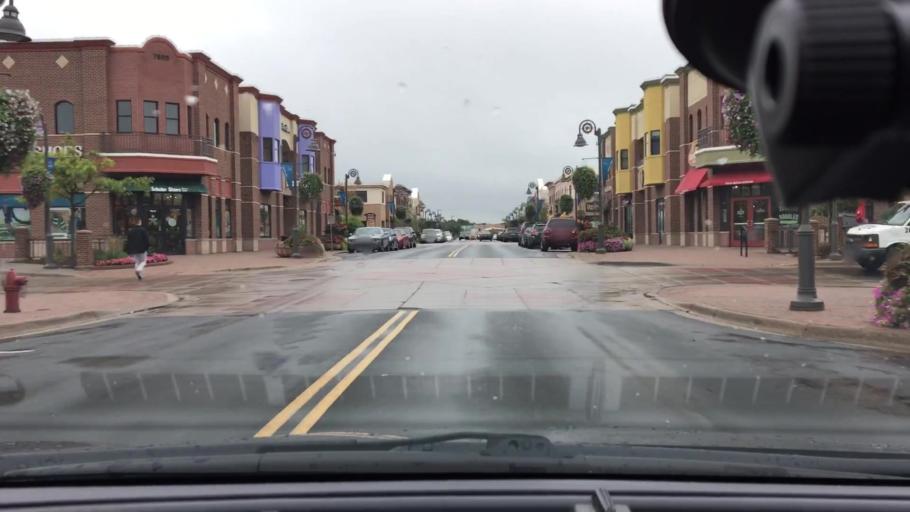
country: US
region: Minnesota
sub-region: Hennepin County
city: Maple Grove
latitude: 45.0964
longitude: -93.4417
